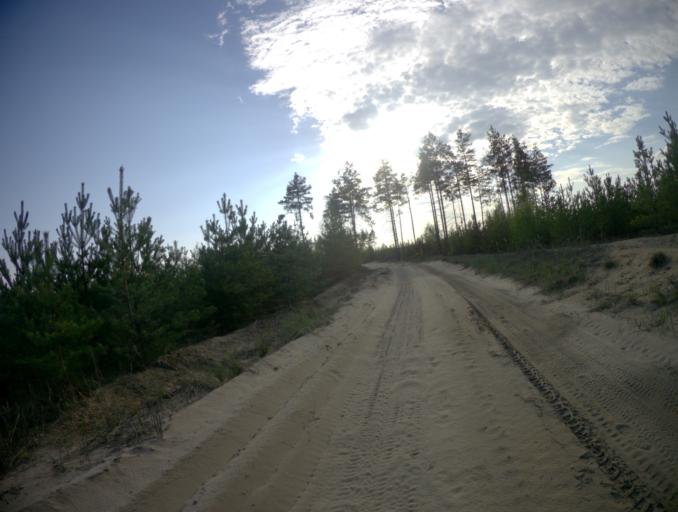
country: RU
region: Vladimir
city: Vyazniki
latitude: 56.4057
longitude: 42.1876
